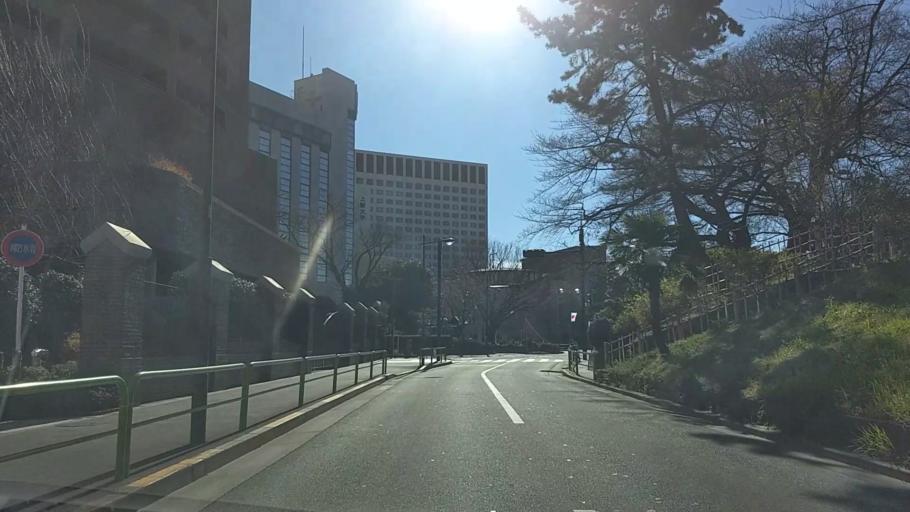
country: JP
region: Tokyo
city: Tokyo
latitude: 35.6867
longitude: 139.7313
